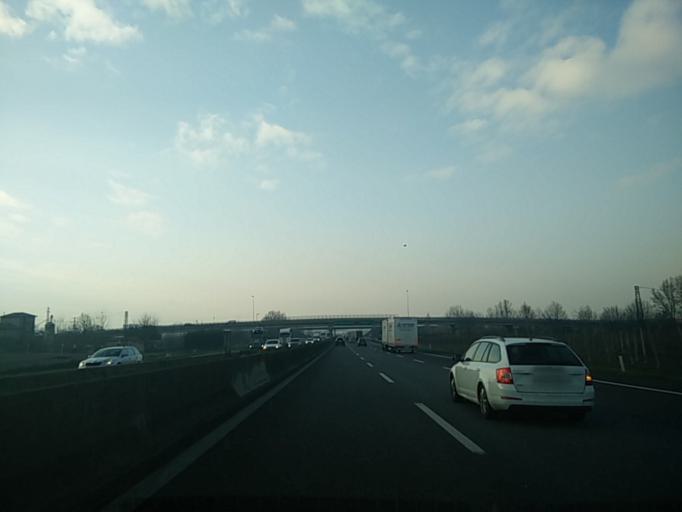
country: IT
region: Emilia-Romagna
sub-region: Provincia di Ravenna
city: Granarolo
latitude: 44.3223
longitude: 11.9087
